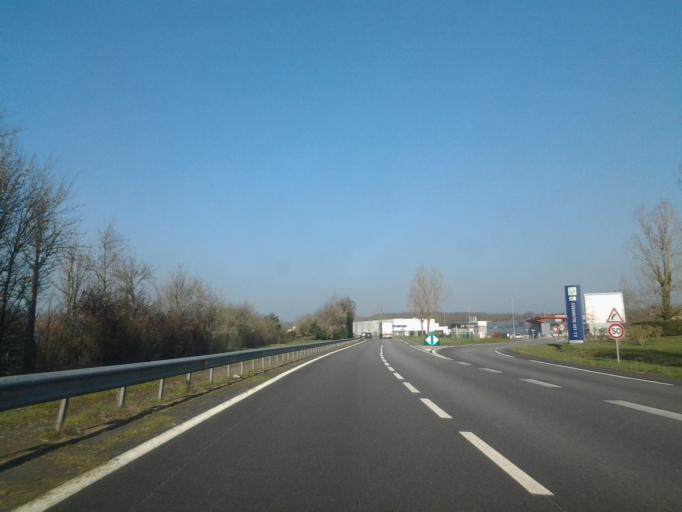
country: FR
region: Pays de la Loire
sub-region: Departement de la Vendee
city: La Genetouze
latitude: 46.7208
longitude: -1.5520
